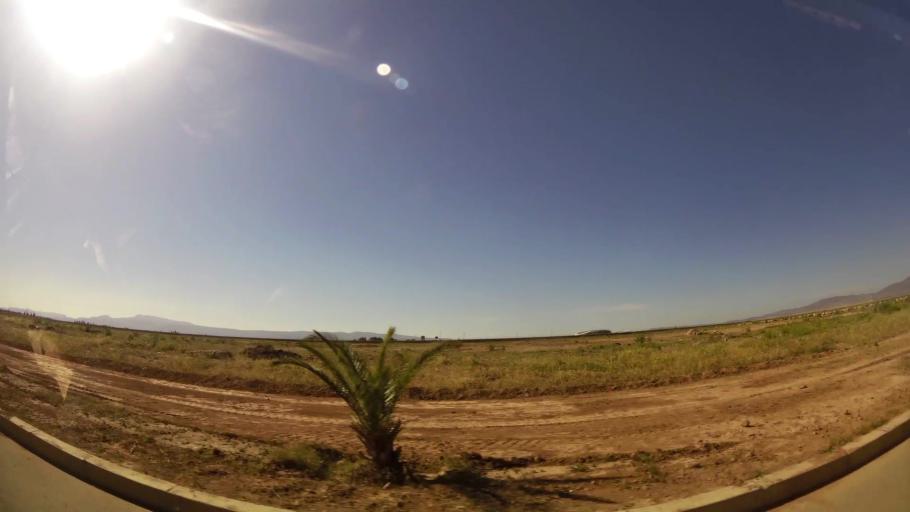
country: MA
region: Oriental
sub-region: Oujda-Angad
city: Oujda
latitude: 34.7757
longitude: -1.9362
